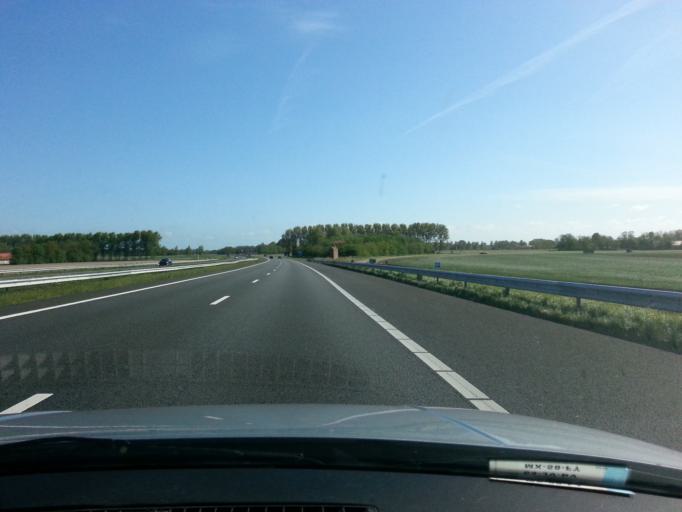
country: NL
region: Flevoland
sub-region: Gemeente Urk
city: Urk
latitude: 52.6181
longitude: 5.6561
